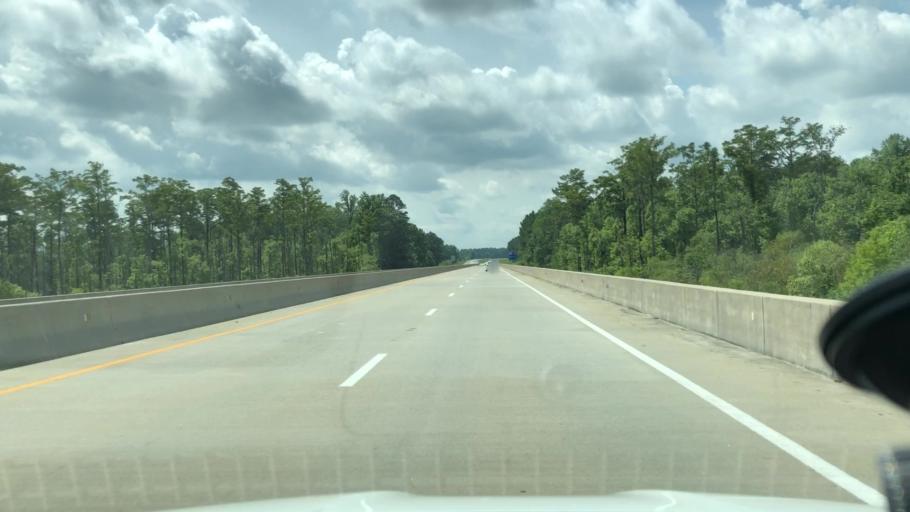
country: US
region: North Carolina
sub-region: Beaufort County
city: Washington
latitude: 35.5221
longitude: -77.0851
